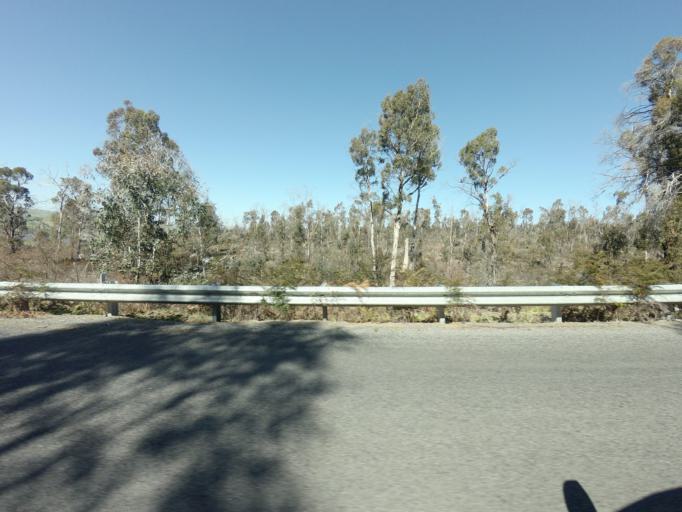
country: AU
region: Tasmania
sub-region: Derwent Valley
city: New Norfolk
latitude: -42.5429
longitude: 146.7185
